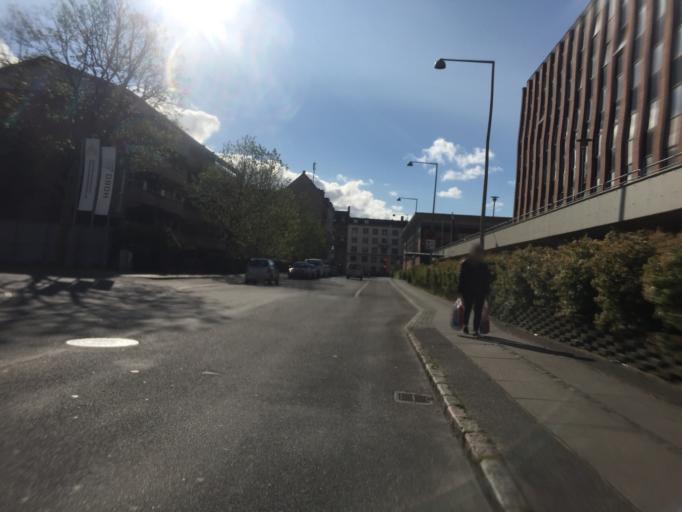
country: DK
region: Capital Region
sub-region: Frederiksberg Kommune
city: Frederiksberg
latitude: 55.6827
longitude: 12.5204
